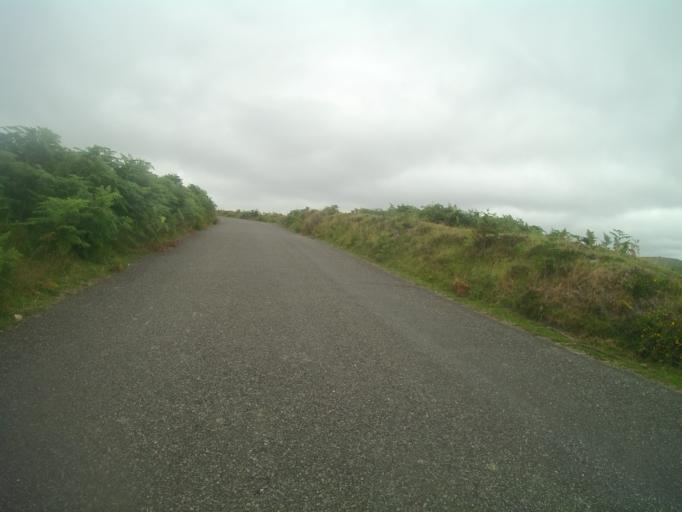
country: GB
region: England
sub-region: Devon
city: Buckfastleigh
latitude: 50.5264
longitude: -3.8590
